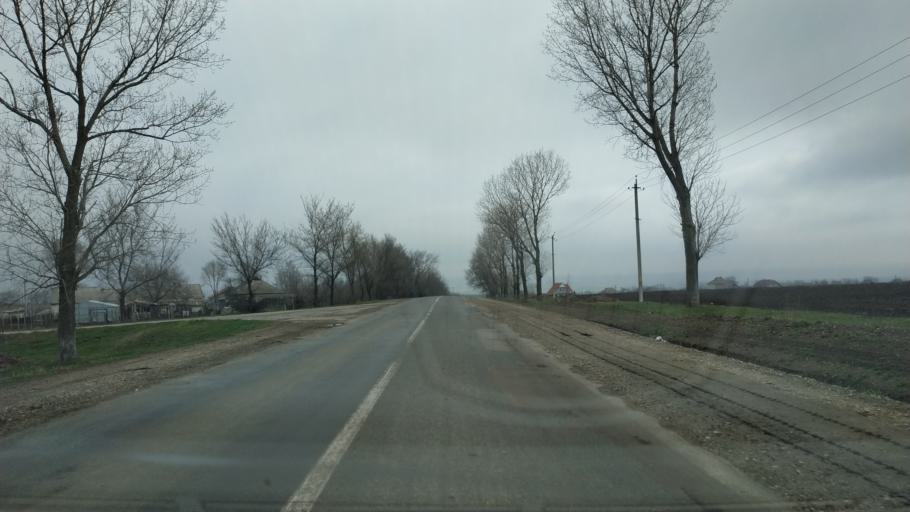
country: MD
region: Straseni
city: Taraclia
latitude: 45.9306
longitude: 28.5734
